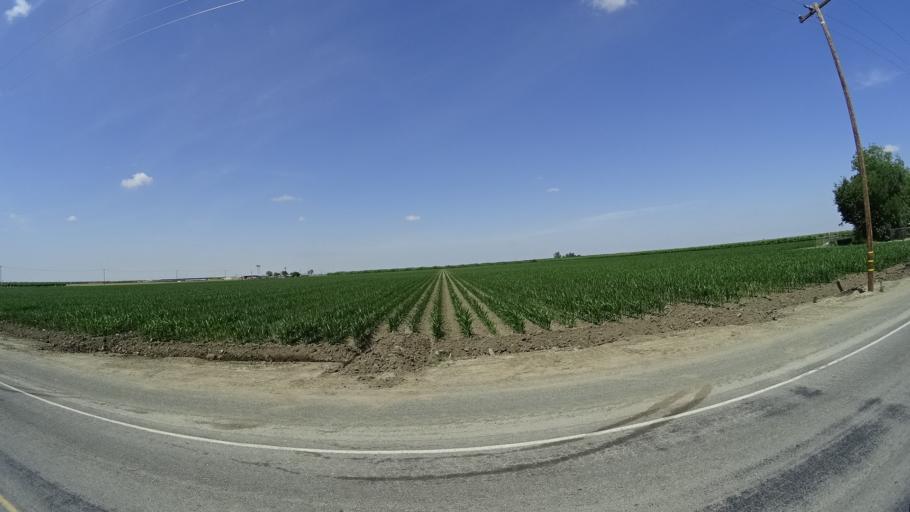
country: US
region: California
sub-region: Tulare County
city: Goshen
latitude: 36.2710
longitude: -119.4923
